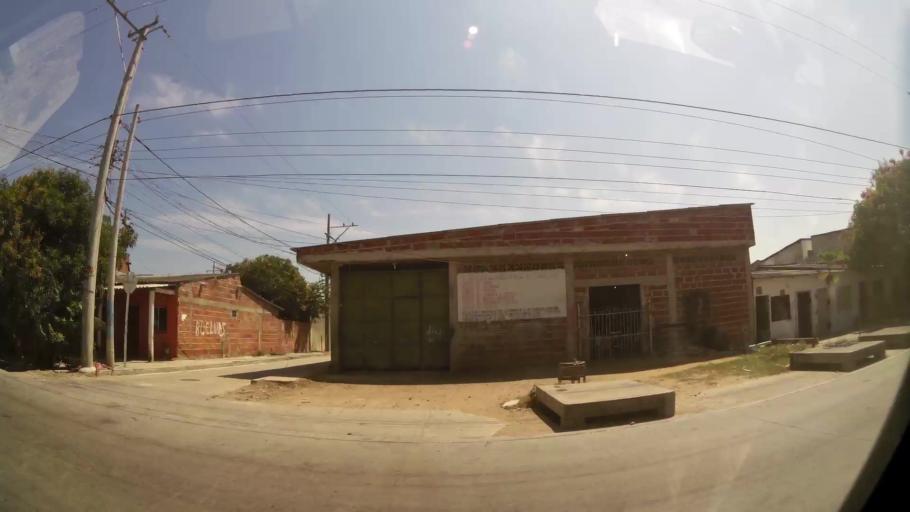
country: CO
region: Atlantico
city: Barranquilla
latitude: 10.9803
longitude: -74.8456
